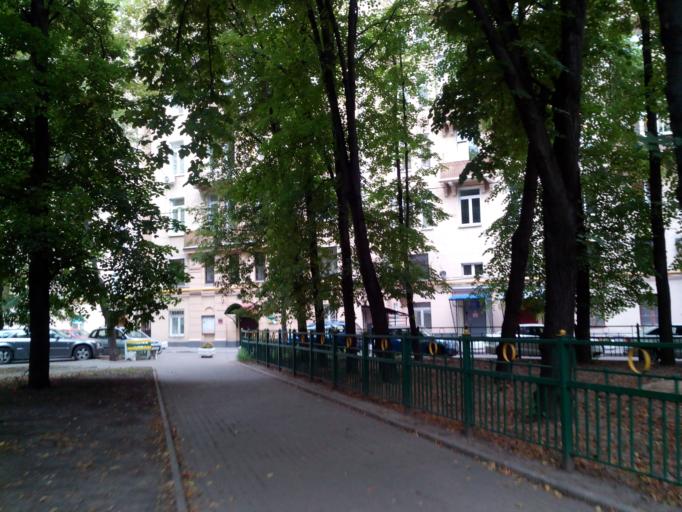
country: RU
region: Moskovskaya
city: Presnenskiy
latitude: 55.7420
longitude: 37.5367
